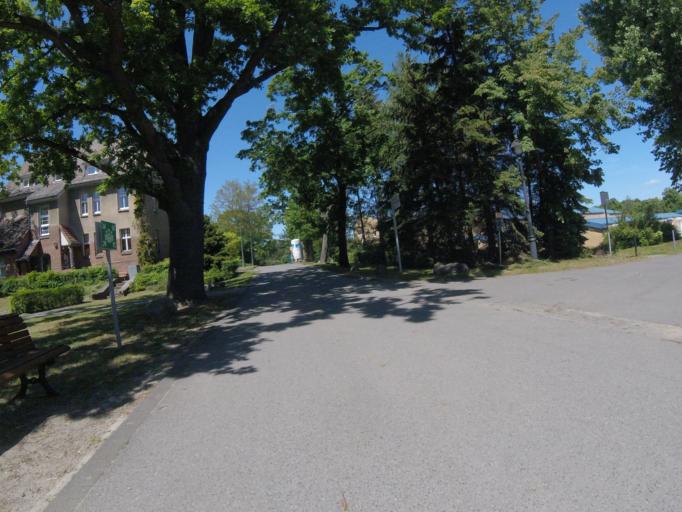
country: DE
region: Brandenburg
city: Teupitz
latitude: 52.1311
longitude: 13.6162
